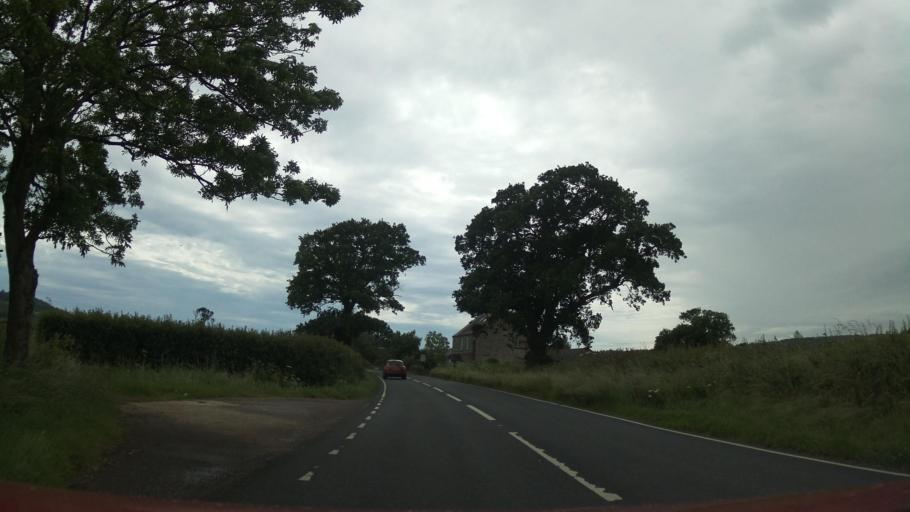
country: GB
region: England
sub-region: Devon
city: Colyton
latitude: 50.7430
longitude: -3.0393
